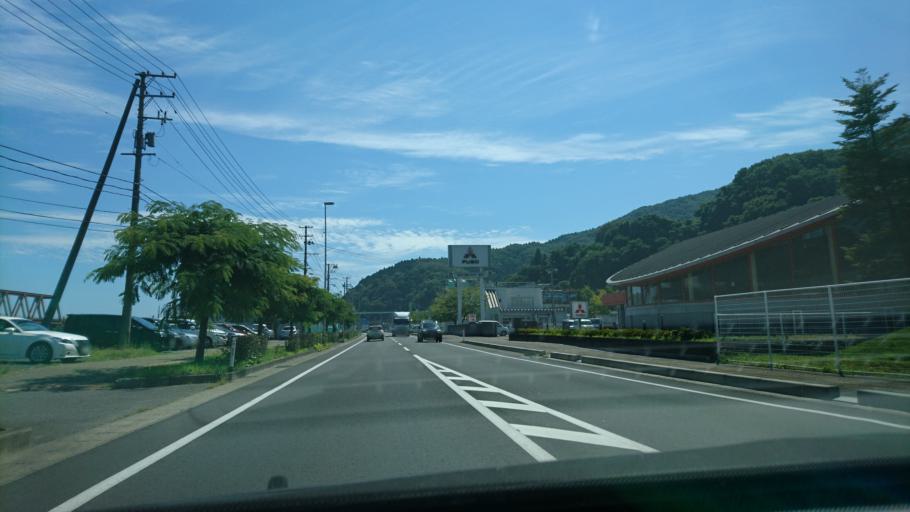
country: JP
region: Iwate
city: Kamaishi
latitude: 39.2691
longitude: 141.8789
